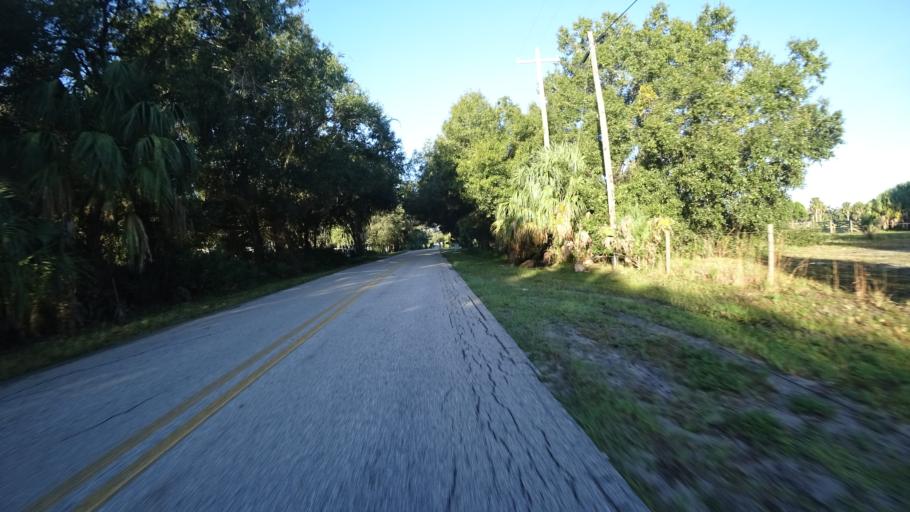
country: US
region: Florida
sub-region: Manatee County
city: Ellenton
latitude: 27.5470
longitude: -82.5330
